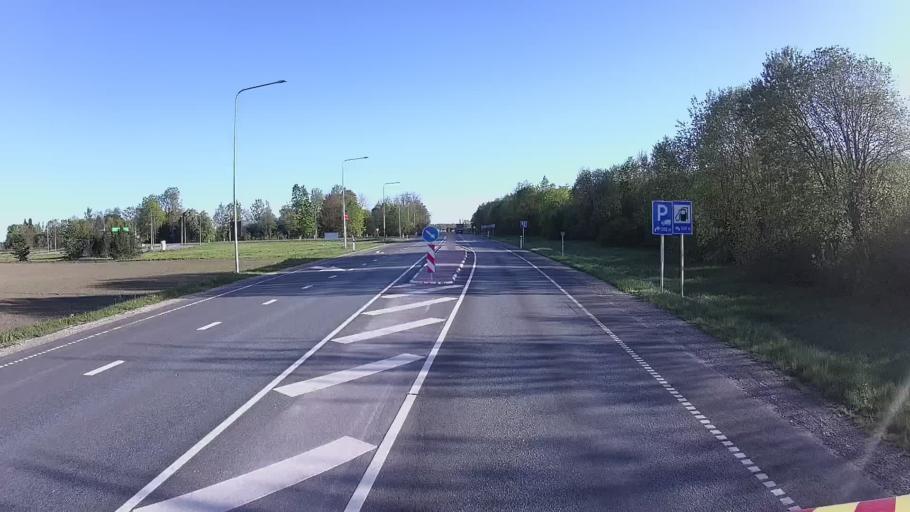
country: EE
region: Viljandimaa
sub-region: Vohma linn
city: Vohma
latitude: 58.6332
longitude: 25.5726
